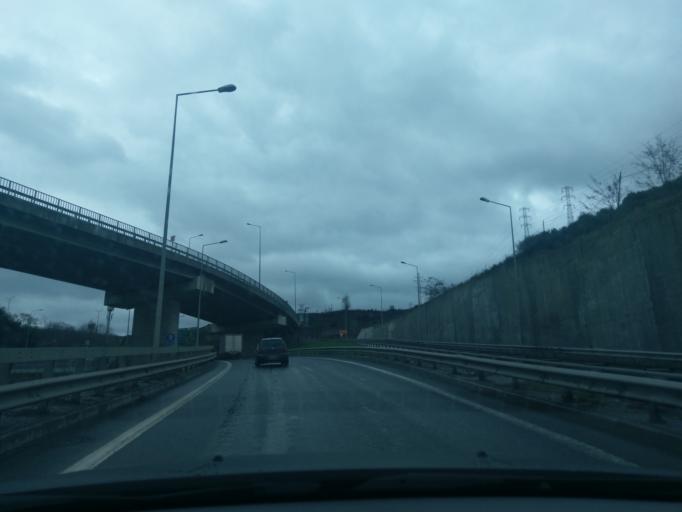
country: TR
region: Istanbul
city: Sisli
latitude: 41.0941
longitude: 28.9534
